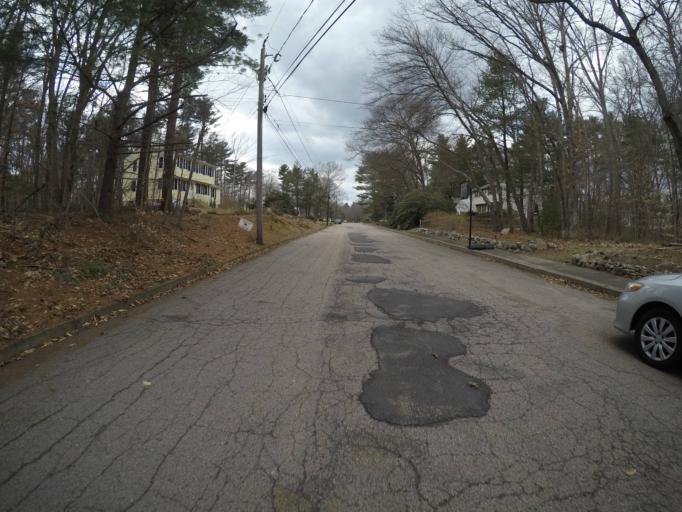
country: US
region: Massachusetts
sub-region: Bristol County
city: Easton
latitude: 42.0481
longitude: -71.1324
